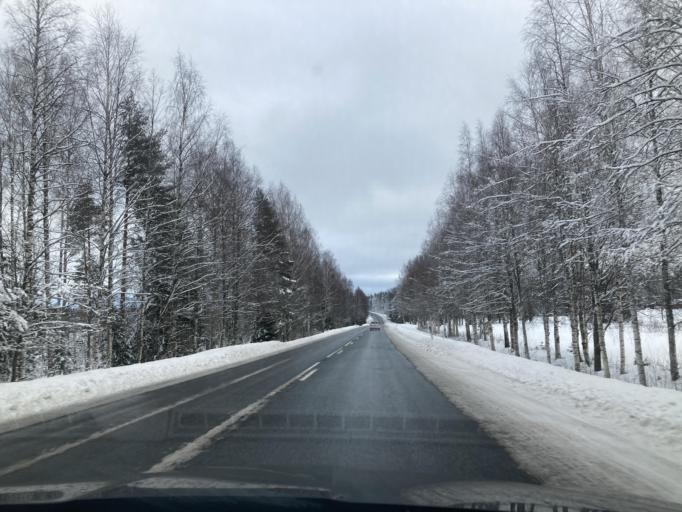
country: FI
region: Paijanne Tavastia
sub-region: Lahti
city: Padasjoki
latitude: 61.3021
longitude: 25.2986
